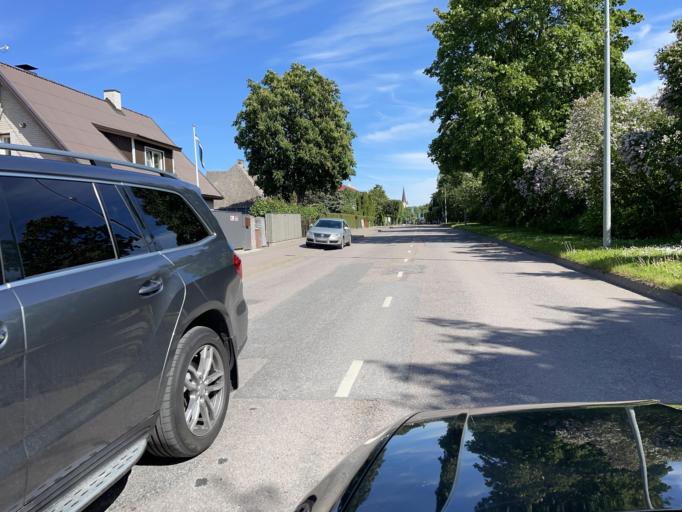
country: EE
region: Harju
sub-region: Keila linn
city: Keila
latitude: 59.3091
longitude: 24.4187
